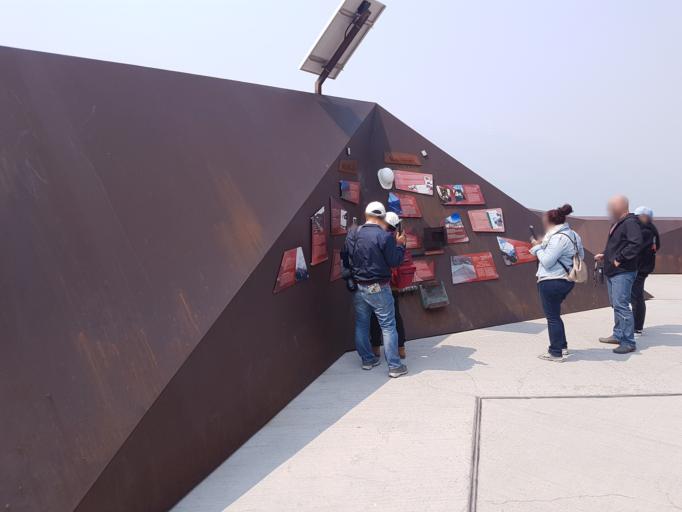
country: CA
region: Alberta
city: Jasper Park Lodge
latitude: 52.2591
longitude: -117.2771
